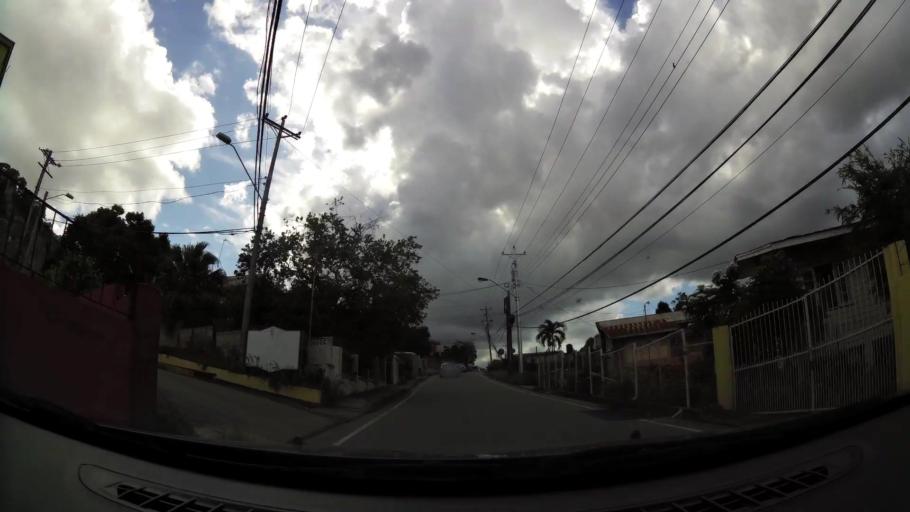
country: TT
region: City of San Fernando
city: San Fernando
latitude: 10.2850
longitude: -61.4568
